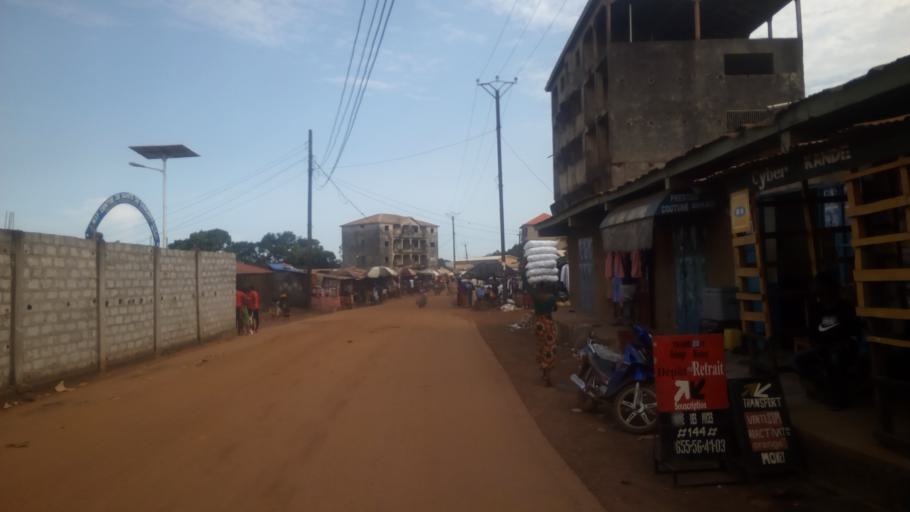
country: GN
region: Kindia
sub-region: Prefecture de Dubreka
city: Dubreka
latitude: 9.6565
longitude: -13.5353
